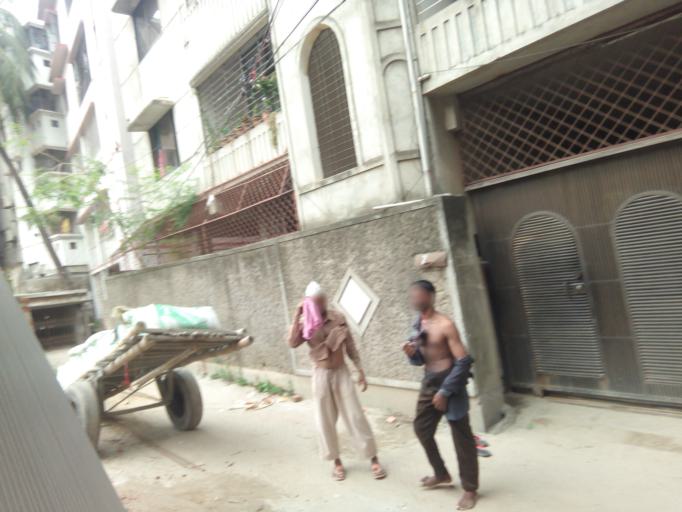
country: BD
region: Dhaka
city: Azimpur
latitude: 23.7519
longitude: 90.3833
